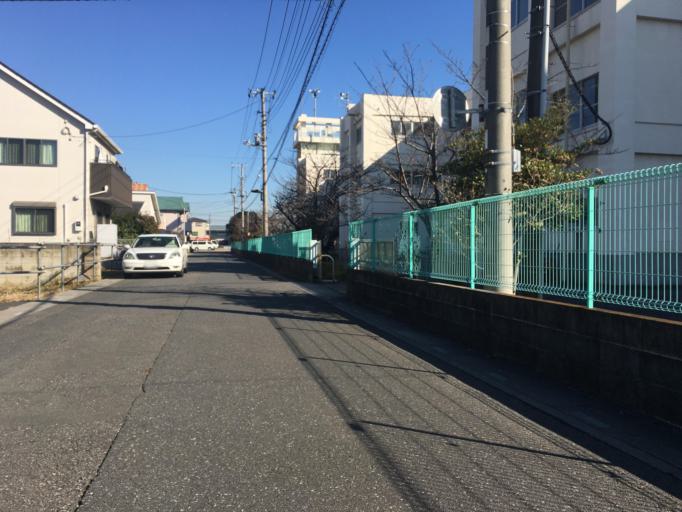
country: JP
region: Saitama
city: Yashio-shi
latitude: 35.8152
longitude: 139.8520
